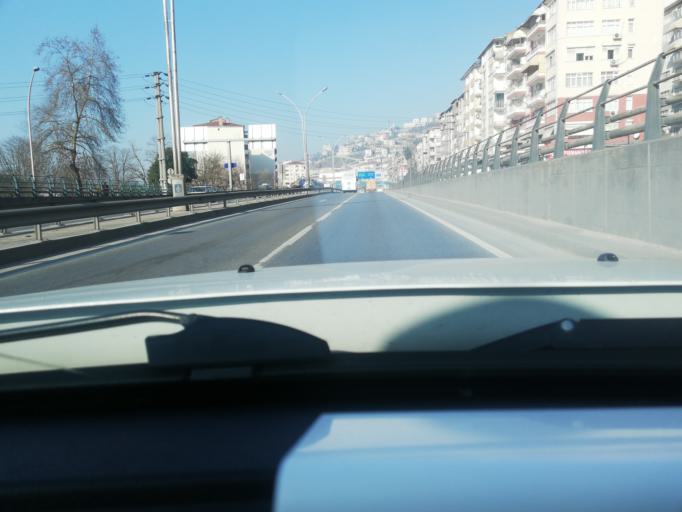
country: TR
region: Kocaeli
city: Izmit
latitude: 40.7664
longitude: 29.9070
